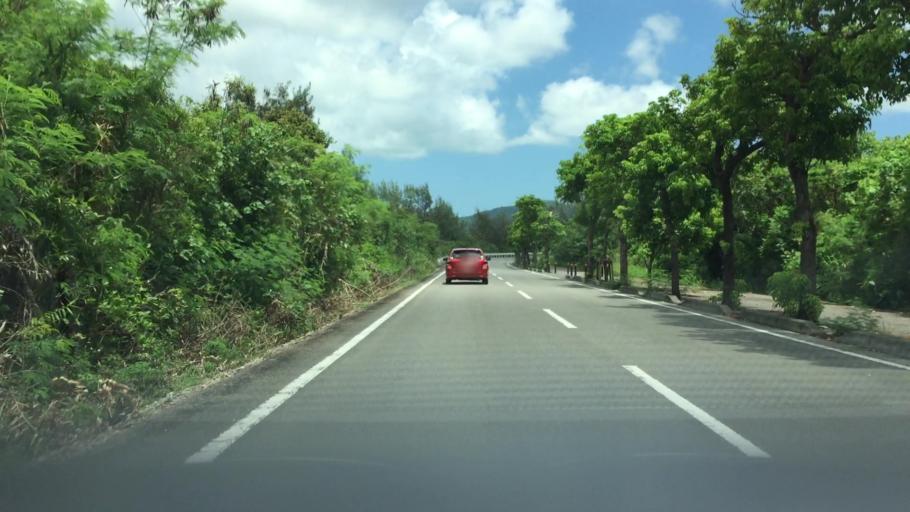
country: JP
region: Okinawa
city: Ishigaki
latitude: 24.3990
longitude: 124.1405
